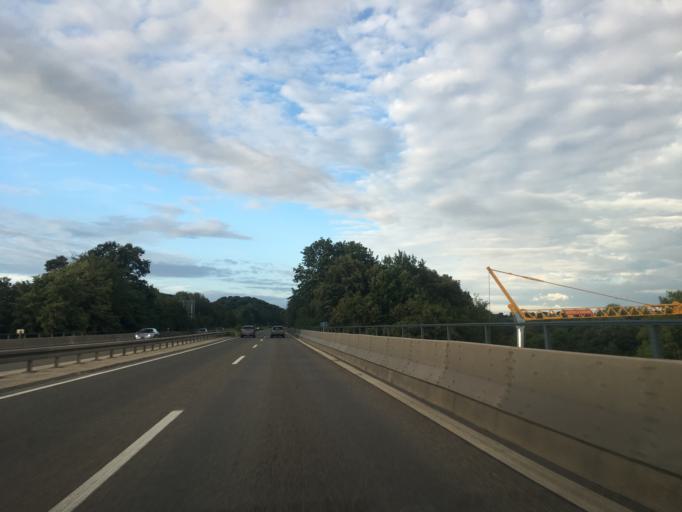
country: DE
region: North Rhine-Westphalia
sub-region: Regierungsbezirk Koln
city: Wurselen
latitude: 50.7914
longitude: 6.1346
